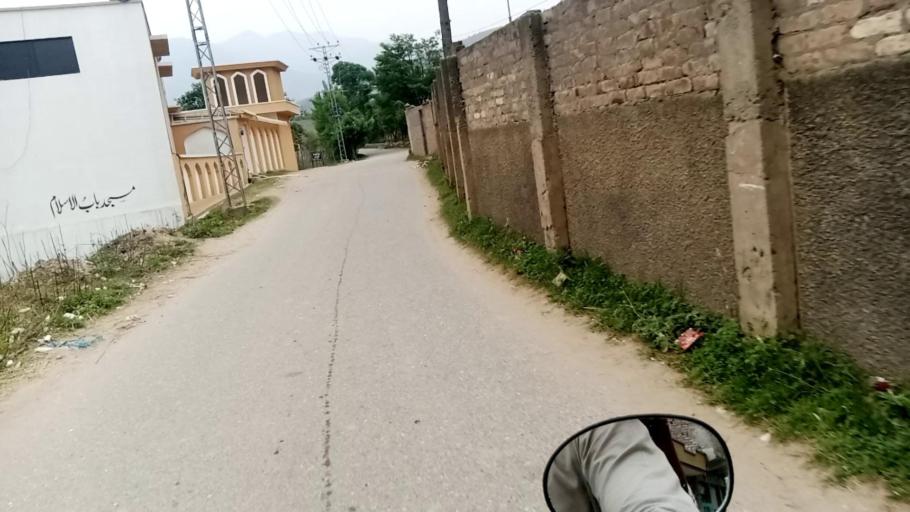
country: PK
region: Khyber Pakhtunkhwa
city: Saidu Sharif
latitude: 34.7558
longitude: 72.3816
